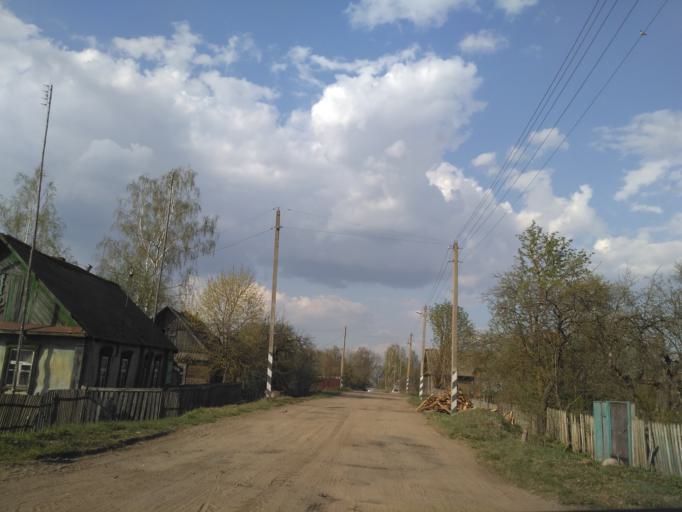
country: BY
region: Minsk
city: Khalopyenichy
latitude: 54.5034
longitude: 28.8484
